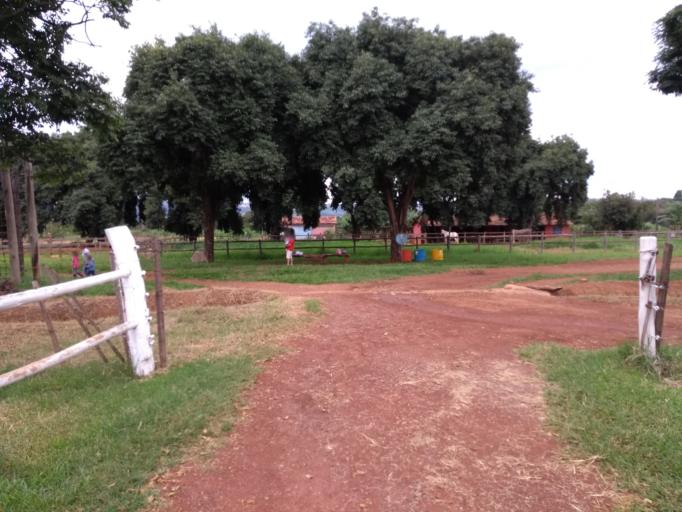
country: BR
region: Federal District
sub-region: Brasilia
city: Brasilia
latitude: -15.6608
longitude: -47.7720
